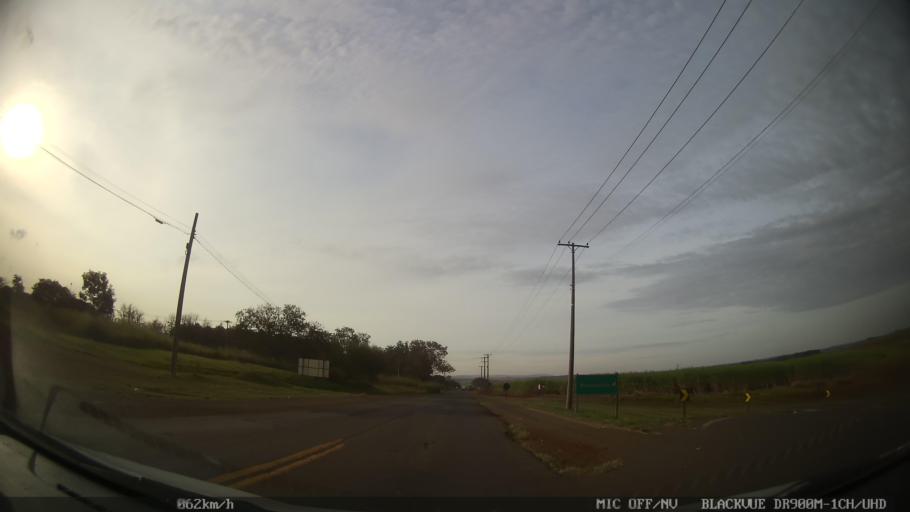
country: BR
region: Sao Paulo
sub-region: Piracicaba
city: Piracicaba
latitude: -22.7224
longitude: -47.5841
